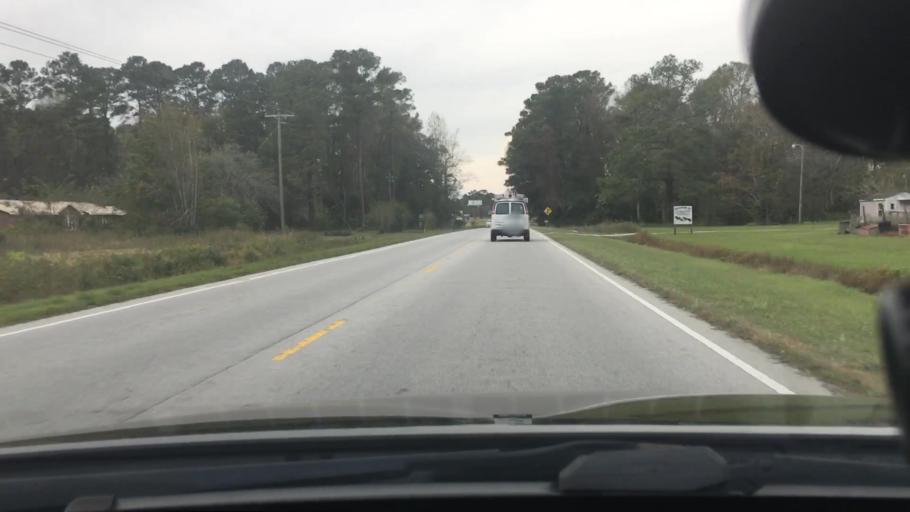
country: US
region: North Carolina
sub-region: Craven County
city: Vanceboro
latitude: 35.2677
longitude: -77.1086
